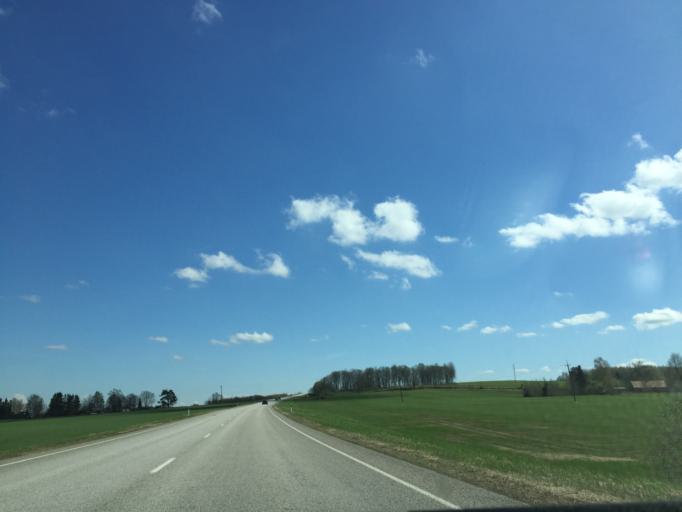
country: EE
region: Valgamaa
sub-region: Valga linn
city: Valga
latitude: 57.9090
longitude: 26.0416
